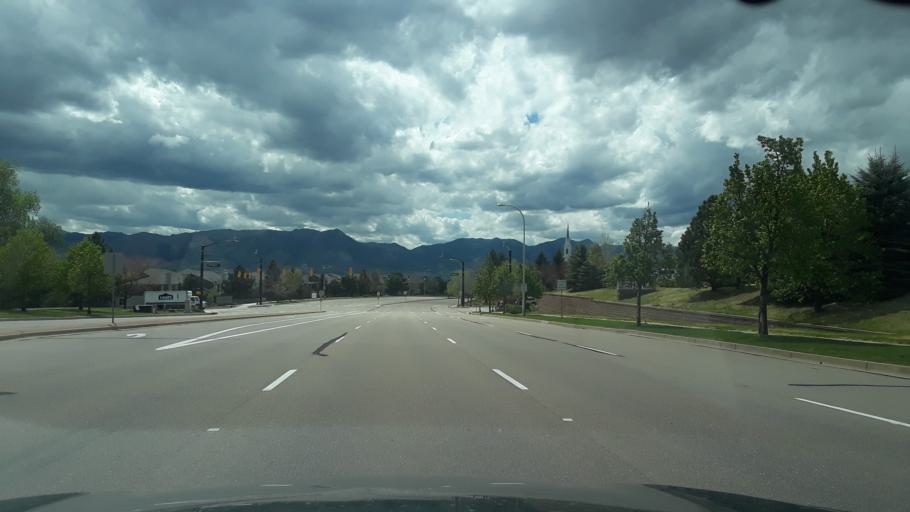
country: US
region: Colorado
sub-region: El Paso County
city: Black Forest
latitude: 38.9570
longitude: -104.7681
